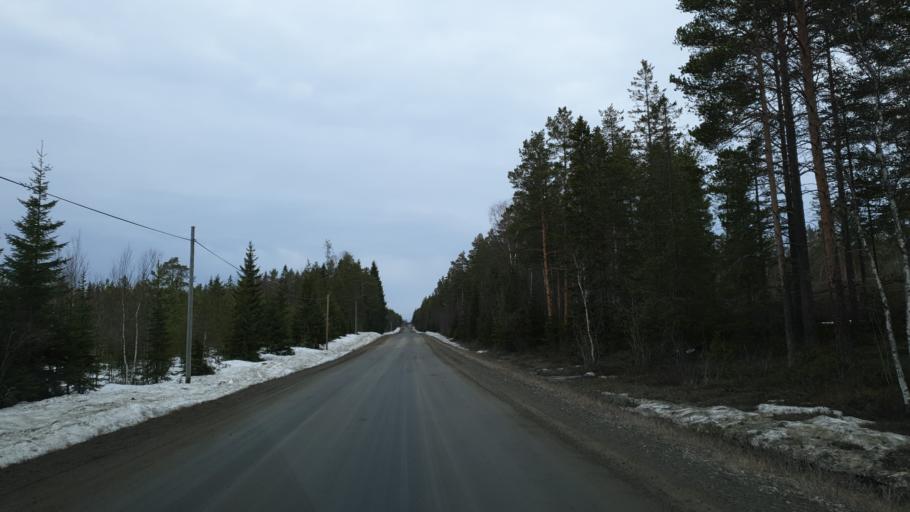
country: SE
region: Vaesterbotten
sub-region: Skelleftea Kommun
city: Burea
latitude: 64.3091
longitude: 21.1433
